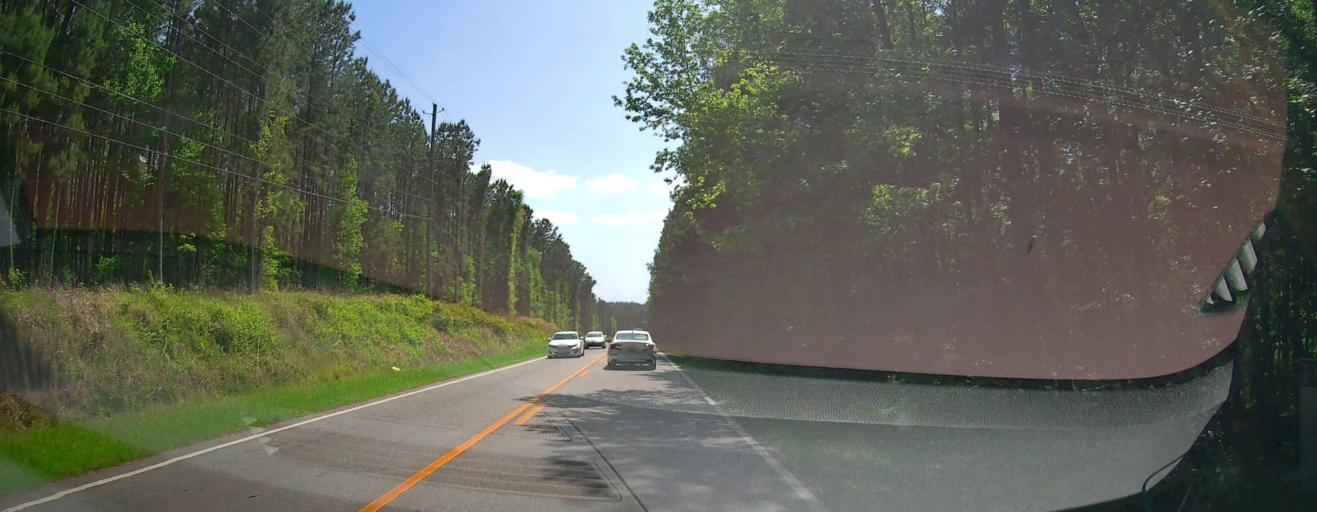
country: US
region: Georgia
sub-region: Putnam County
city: Eatonton
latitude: 33.2438
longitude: -83.3055
